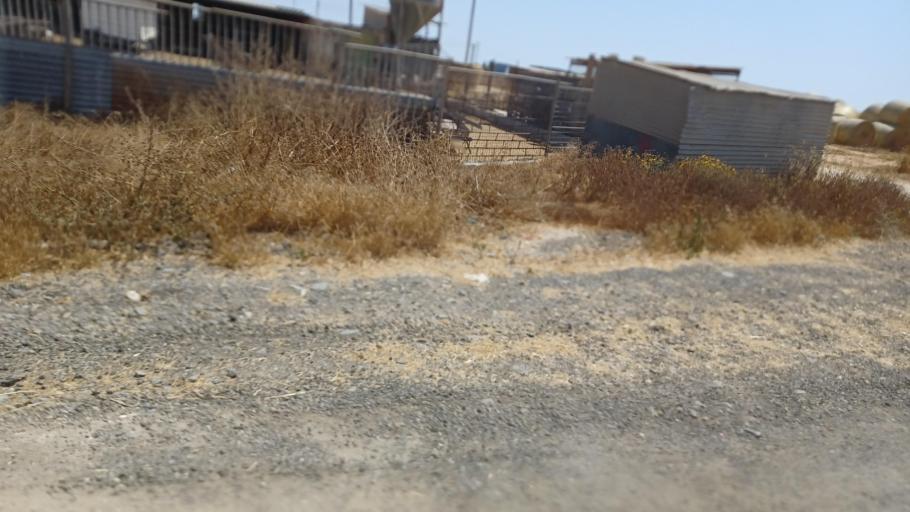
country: CY
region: Ammochostos
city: Frenaros
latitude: 35.0088
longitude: 33.9421
